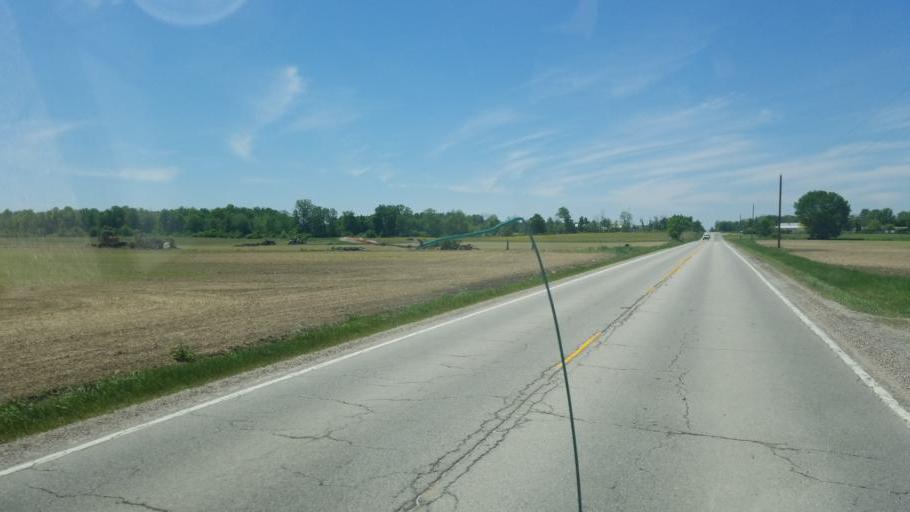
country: US
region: Ohio
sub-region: Huron County
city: New London
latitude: 41.0293
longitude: -82.4434
